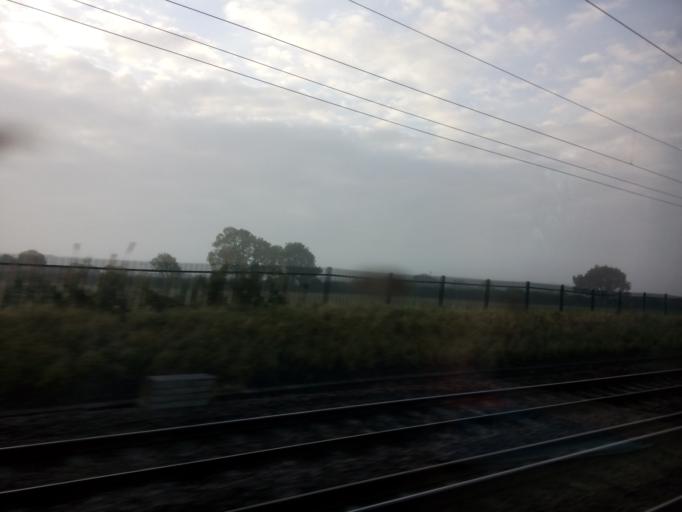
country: GB
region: England
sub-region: City of York
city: Copmanthorpe
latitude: 53.9058
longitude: -1.1468
